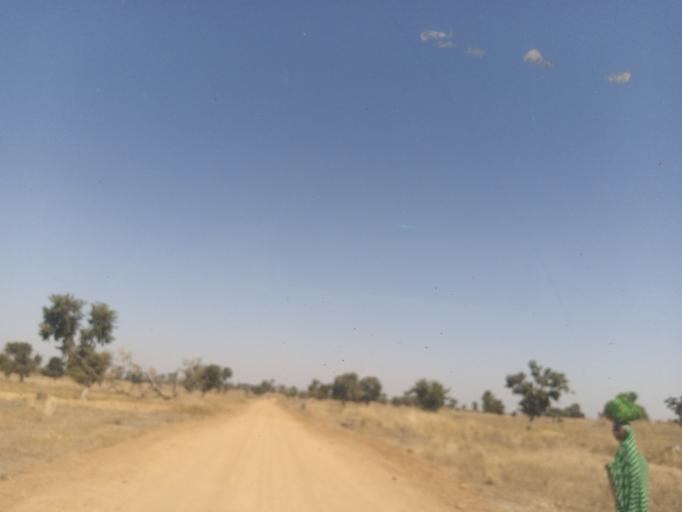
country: NG
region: Adamawa
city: Yola
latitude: 9.2925
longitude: 12.8857
